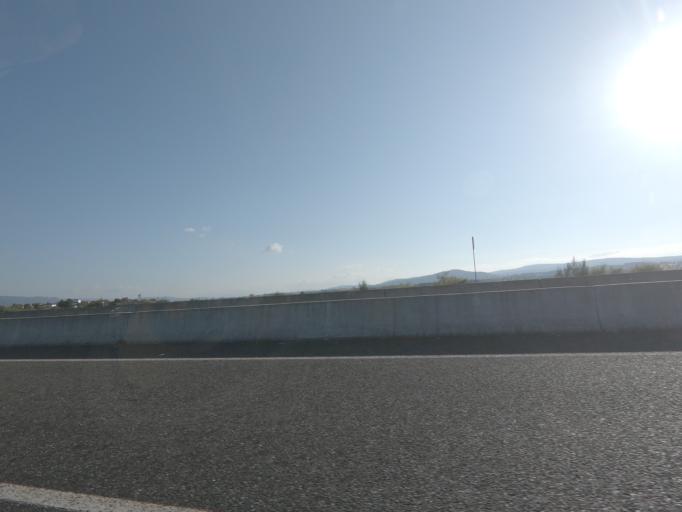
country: ES
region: Galicia
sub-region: Provincia de Ourense
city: Oimbra
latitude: 41.8203
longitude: -7.4181
